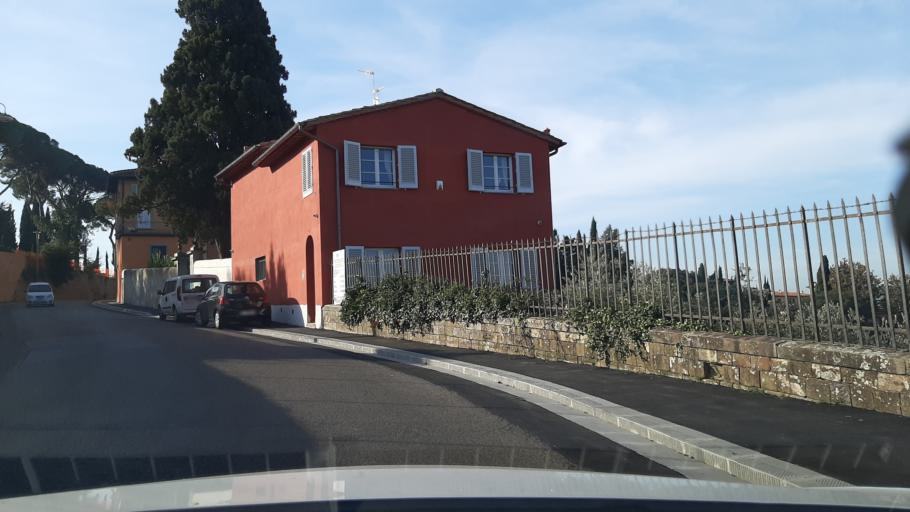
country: IT
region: Tuscany
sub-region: Province of Florence
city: Florence
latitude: 43.7532
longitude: 11.2571
